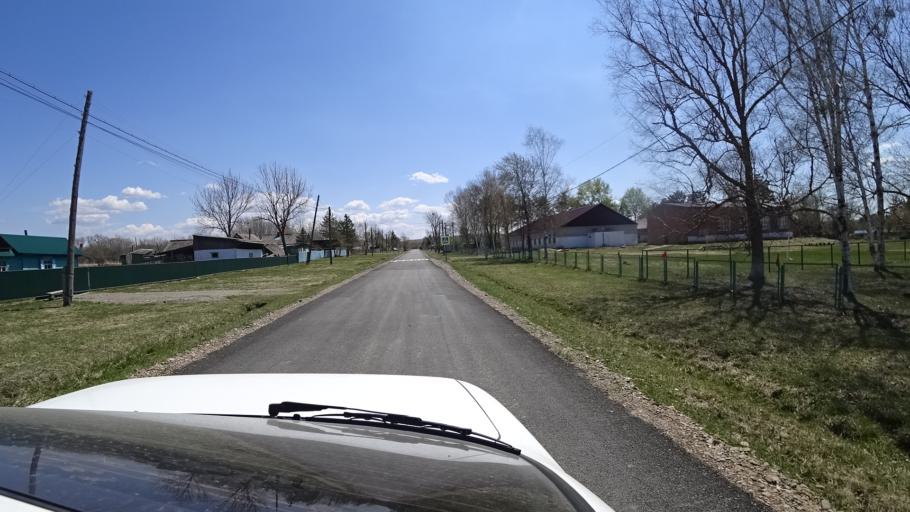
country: RU
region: Primorskiy
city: Dal'nerechensk
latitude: 45.7955
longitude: 133.7682
